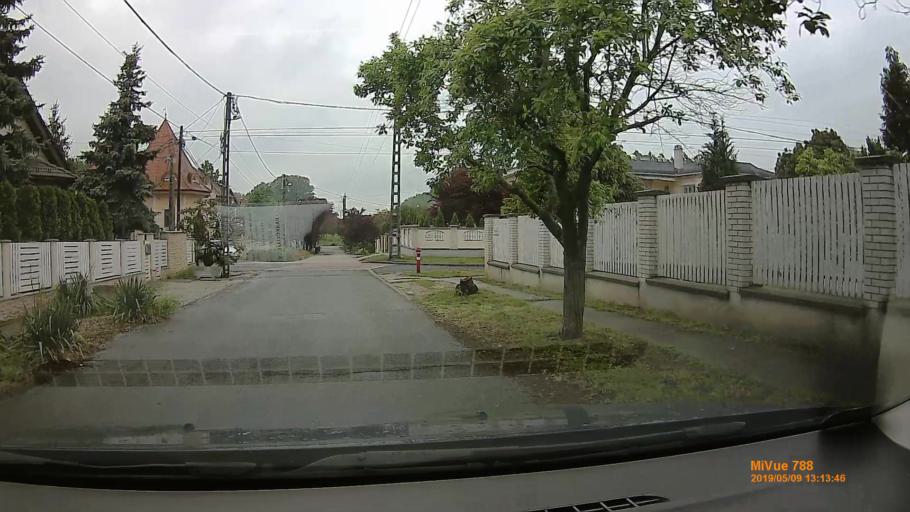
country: HU
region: Budapest
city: Budapest XVI. keruelet
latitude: 47.5408
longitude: 19.1815
